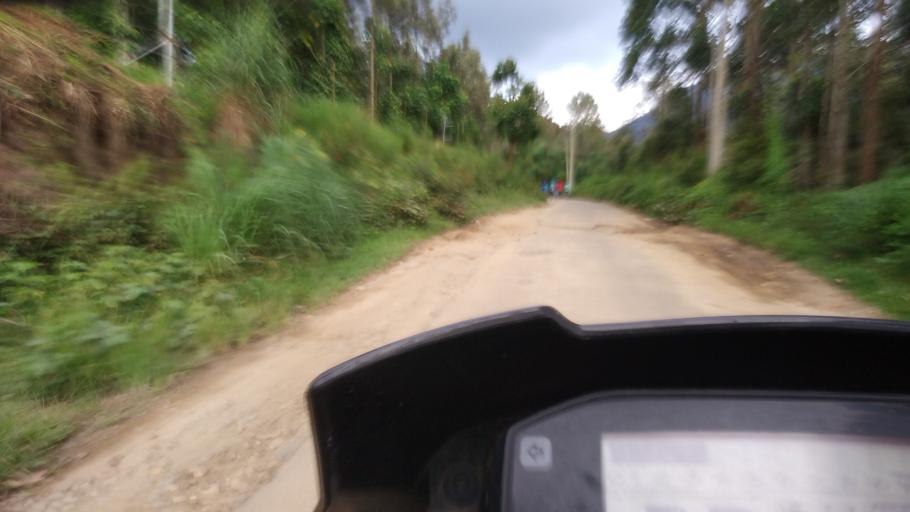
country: IN
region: Tamil Nadu
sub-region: Theni
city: Bodinayakkanur
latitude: 10.0247
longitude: 77.2331
